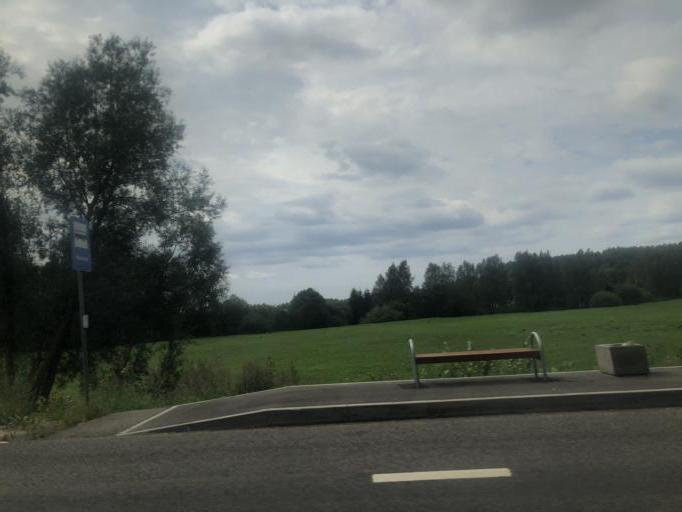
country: LV
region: Baldone
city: Baldone
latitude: 56.7161
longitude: 24.3729
